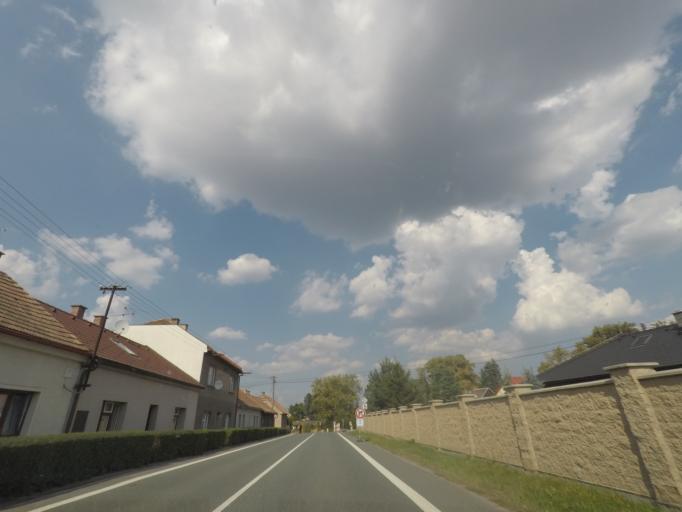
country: CZ
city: Borohradek
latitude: 50.0923
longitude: 16.0890
